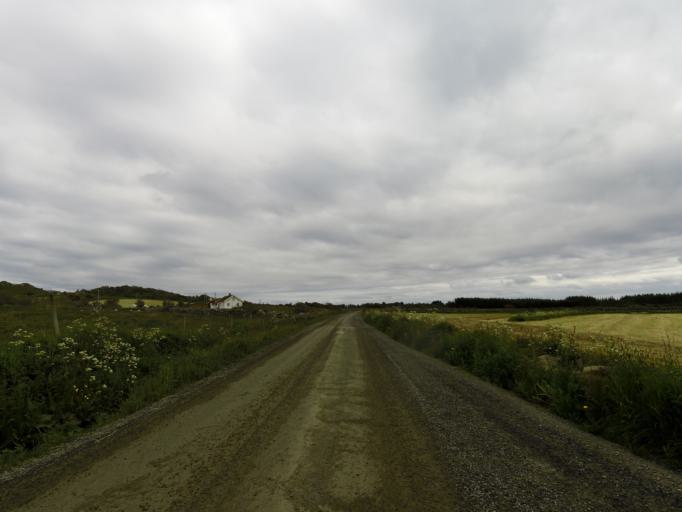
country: NO
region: Vest-Agder
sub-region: Farsund
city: Vestbygd
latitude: 58.1345
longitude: 6.6076
